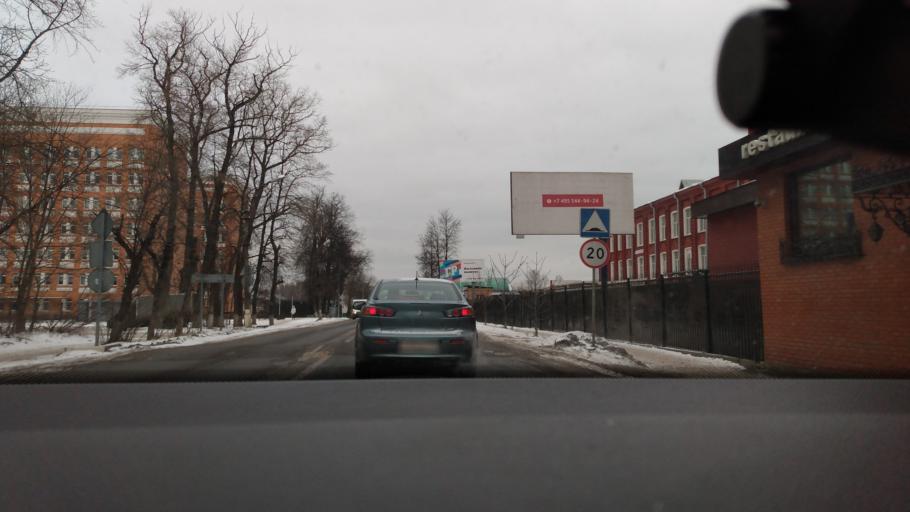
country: RU
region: Moskovskaya
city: Zheleznodorozhnyy
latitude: 55.7283
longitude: 38.0310
